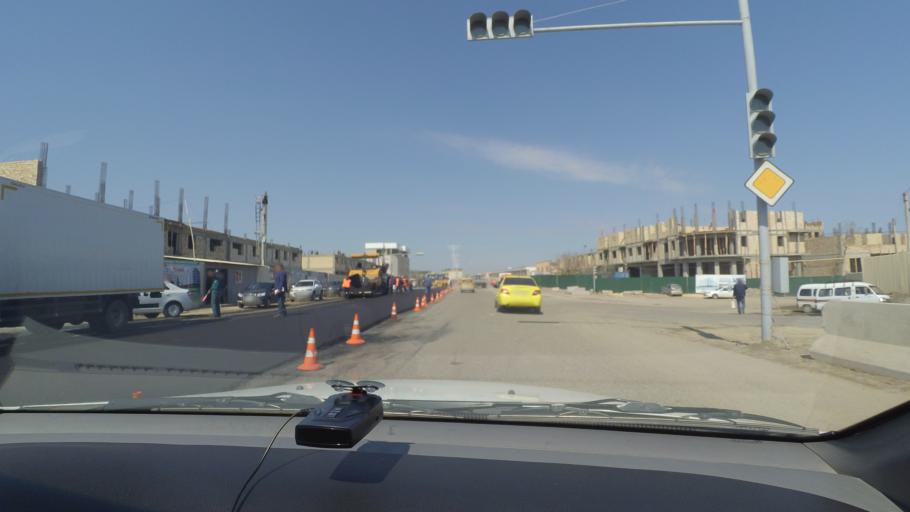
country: UZ
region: Bukhara
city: Bukhara
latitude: 39.7771
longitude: 64.4435
